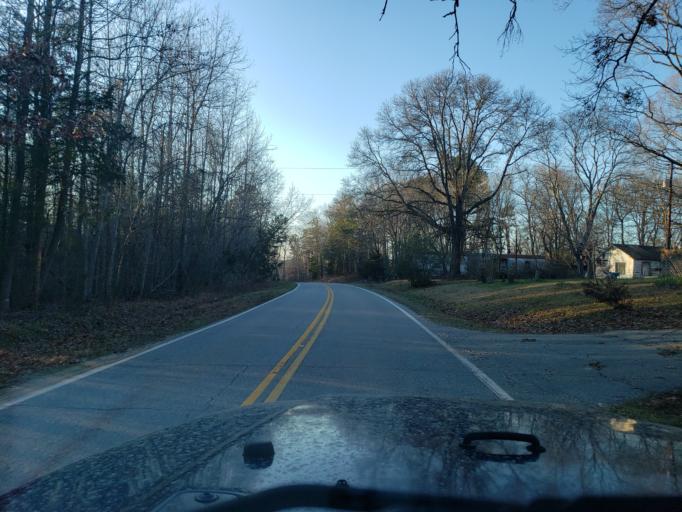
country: US
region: South Carolina
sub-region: Cherokee County
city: Blacksburg
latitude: 35.0665
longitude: -81.4343
